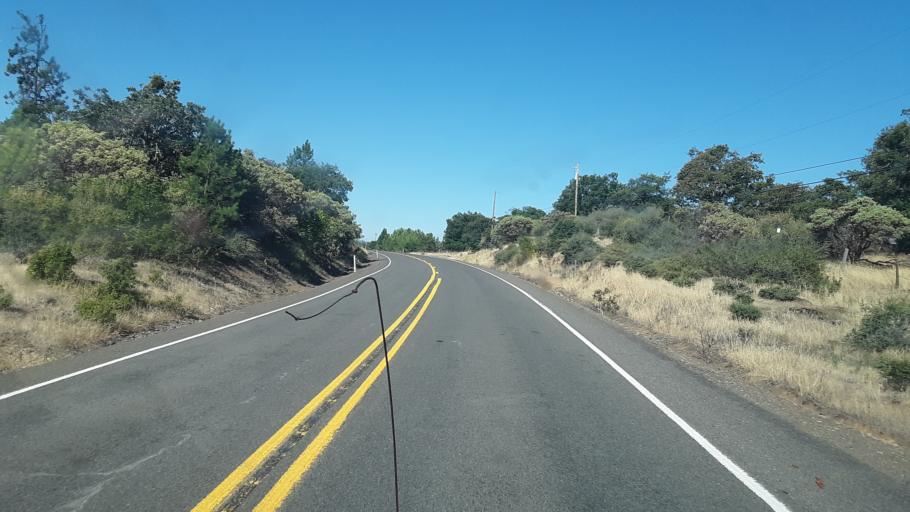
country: US
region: Oregon
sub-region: Jackson County
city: Eagle Point
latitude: 42.5257
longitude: -122.8484
